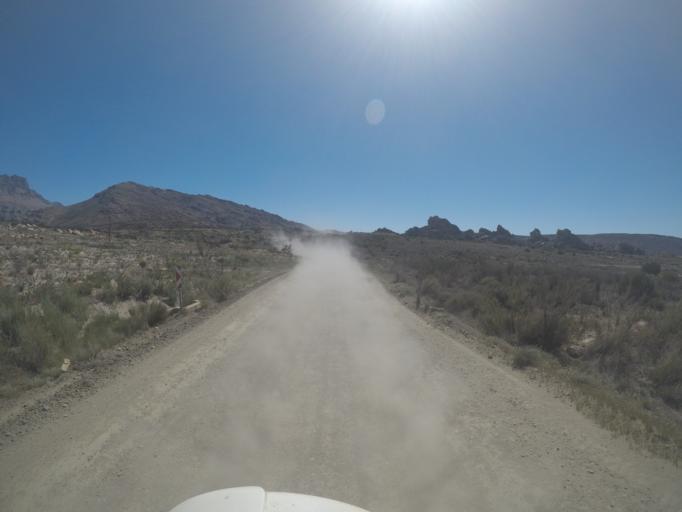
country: ZA
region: Western Cape
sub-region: Cape Winelands District Municipality
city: Ceres
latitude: -32.8580
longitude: 19.4441
